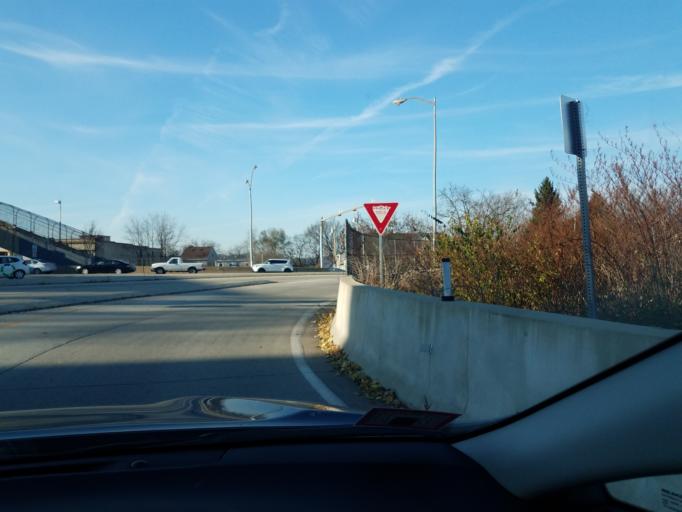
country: US
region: Pennsylvania
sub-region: Allegheny County
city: Bloomfield
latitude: 40.4586
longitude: -79.9569
